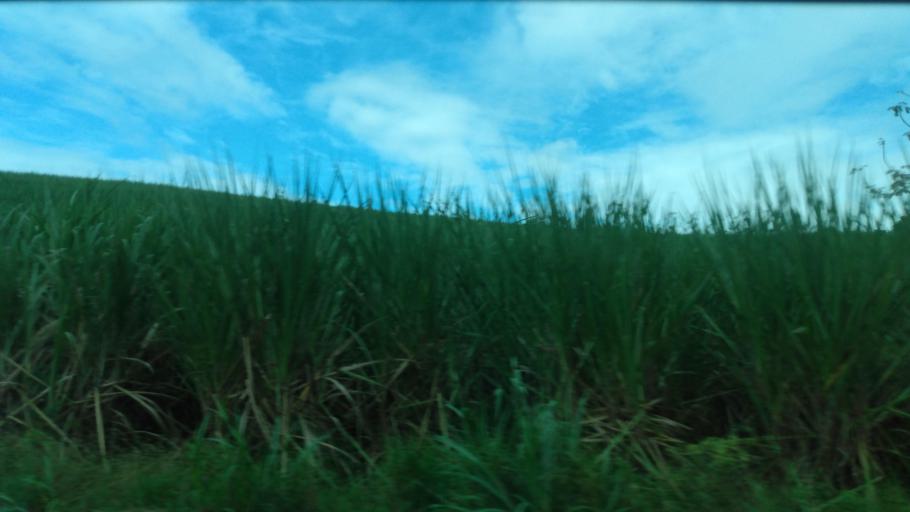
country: BR
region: Pernambuco
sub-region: Maraial
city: Maraial
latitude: -8.7152
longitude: -35.7764
